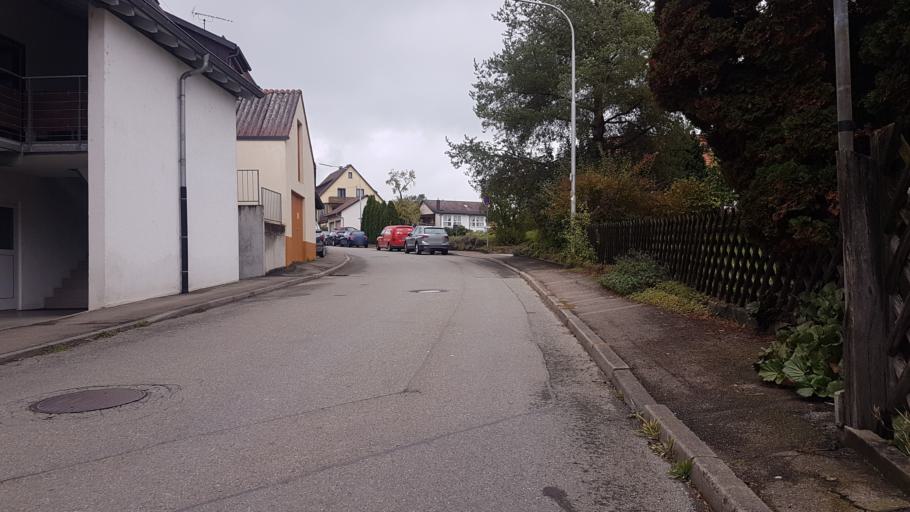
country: DE
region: Baden-Wuerttemberg
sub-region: Tuebingen Region
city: Ofterdingen
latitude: 48.4240
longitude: 9.0350
